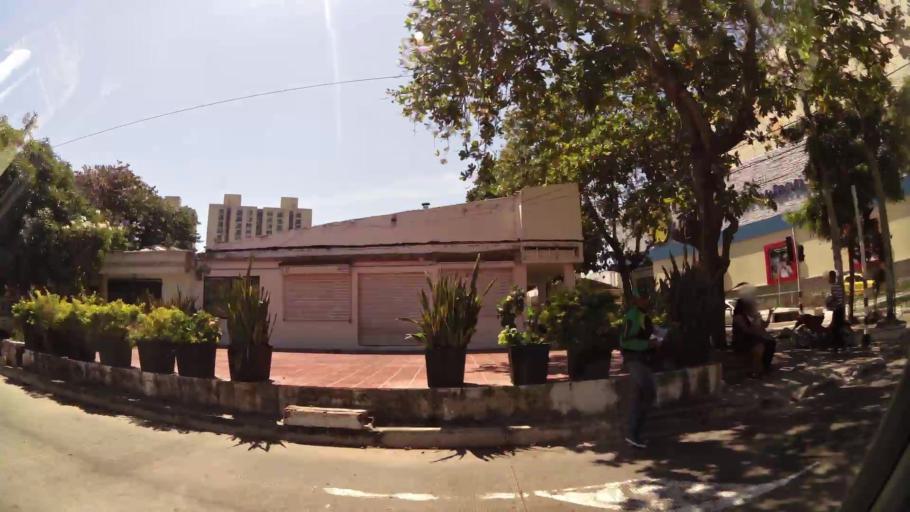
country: CO
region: Atlantico
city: Barranquilla
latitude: 10.9886
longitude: -74.8117
